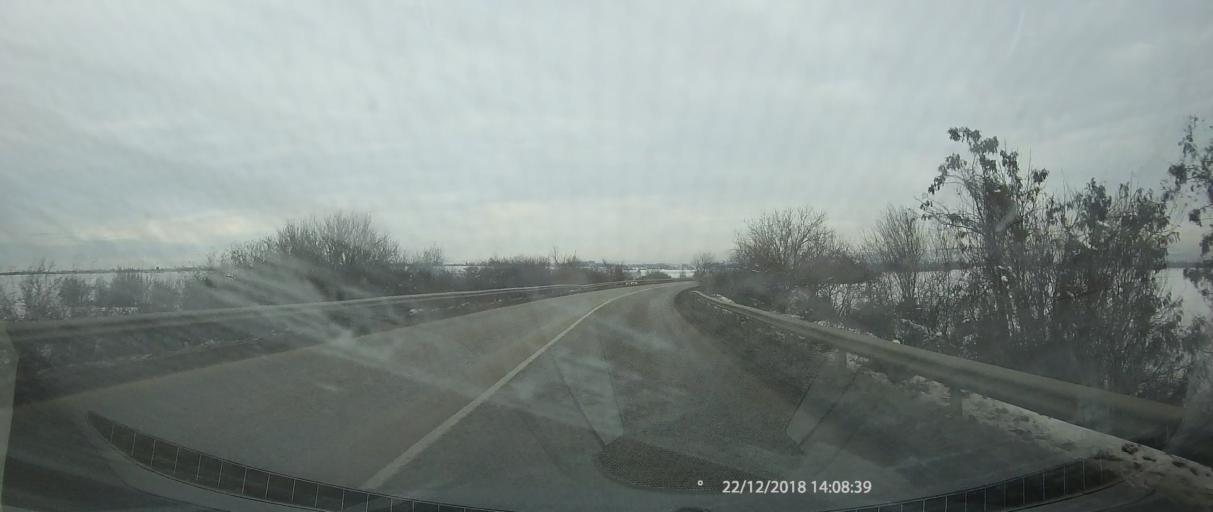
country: BG
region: Pleven
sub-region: Obshtina Dolna Mitropoliya
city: Dolna Mitropoliya
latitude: 43.4293
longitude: 24.5025
